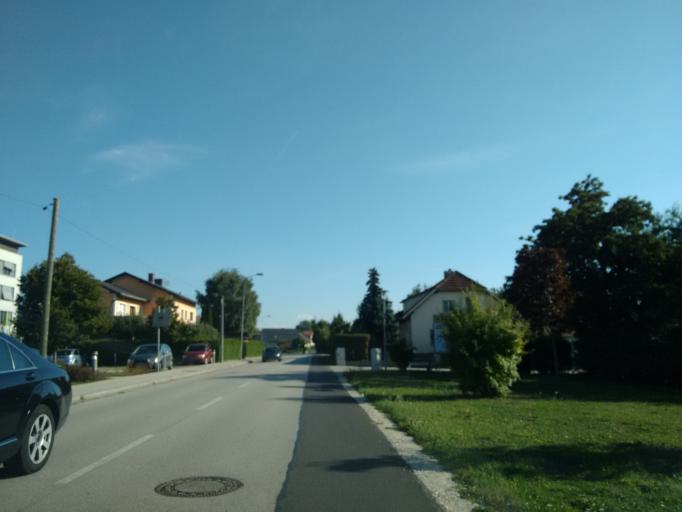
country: AT
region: Upper Austria
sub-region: Wels-Land
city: Marchtrenk
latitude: 48.1805
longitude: 14.1158
